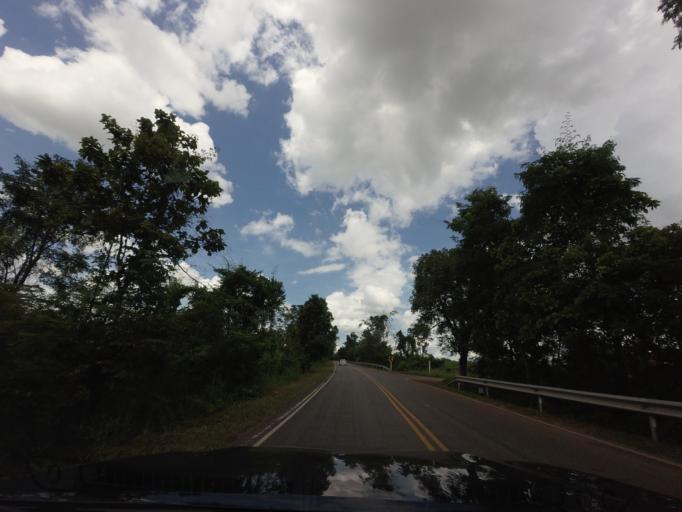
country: TH
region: Changwat Udon Thani
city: Phibun Rak
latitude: 17.6092
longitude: 103.0782
